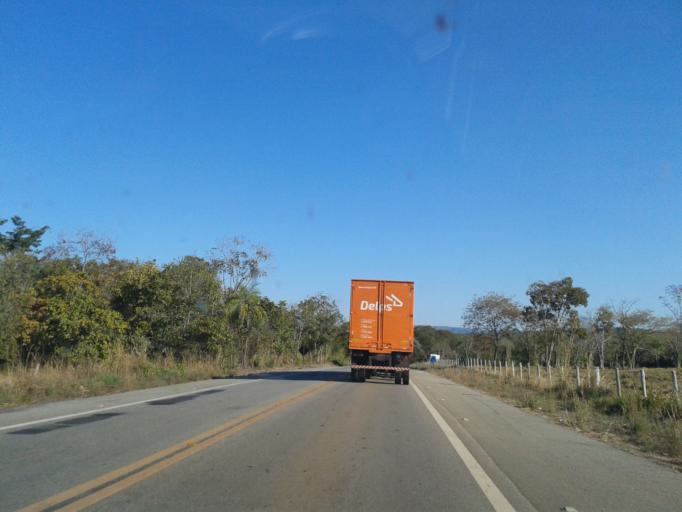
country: BR
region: Goias
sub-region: Itapirapua
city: Itapirapua
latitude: -15.3093
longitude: -50.4433
